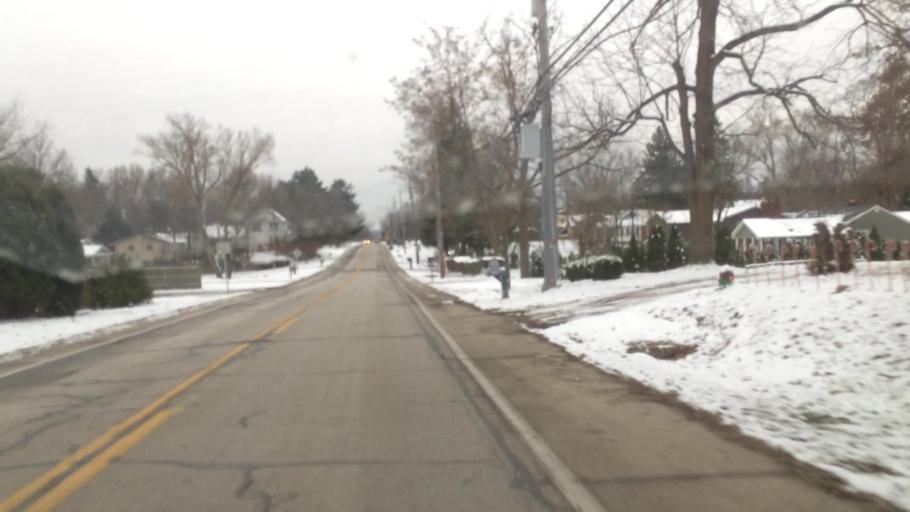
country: US
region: Ohio
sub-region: Cuyahoga County
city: Middleburg Heights
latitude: 41.3424
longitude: -81.8007
